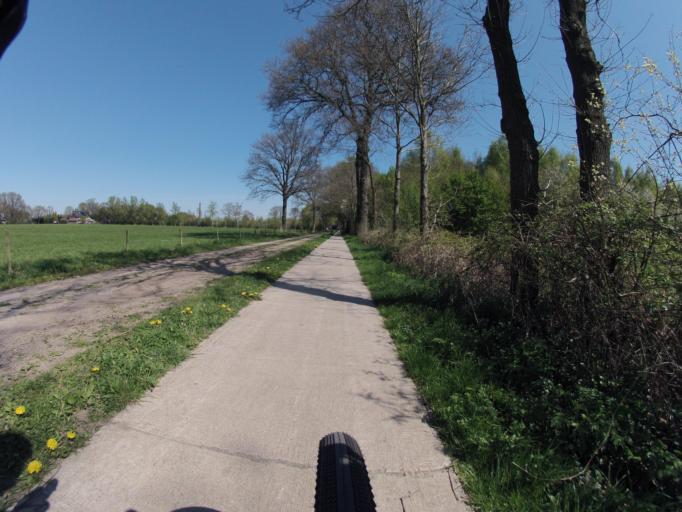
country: NL
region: Overijssel
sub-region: Gemeente Losser
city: Losser
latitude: 52.2666
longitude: 6.9839
